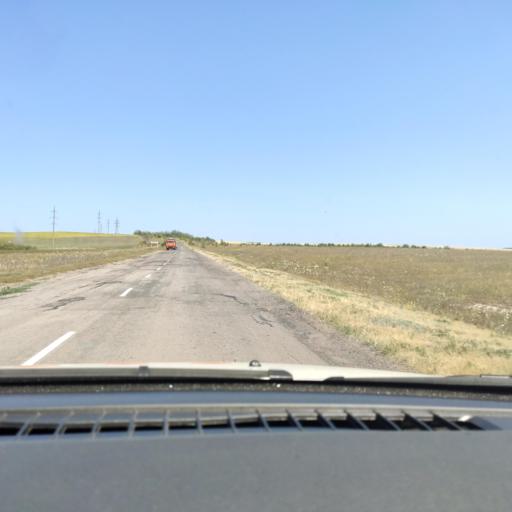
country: RU
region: Voronezj
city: Ol'khovatka
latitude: 50.5798
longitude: 39.2733
